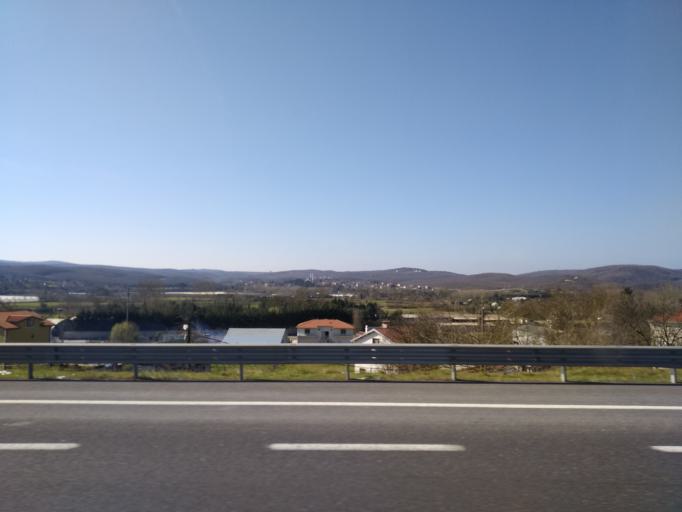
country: TR
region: Istanbul
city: Mahmut Sevket Pasa
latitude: 41.1293
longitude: 29.2861
